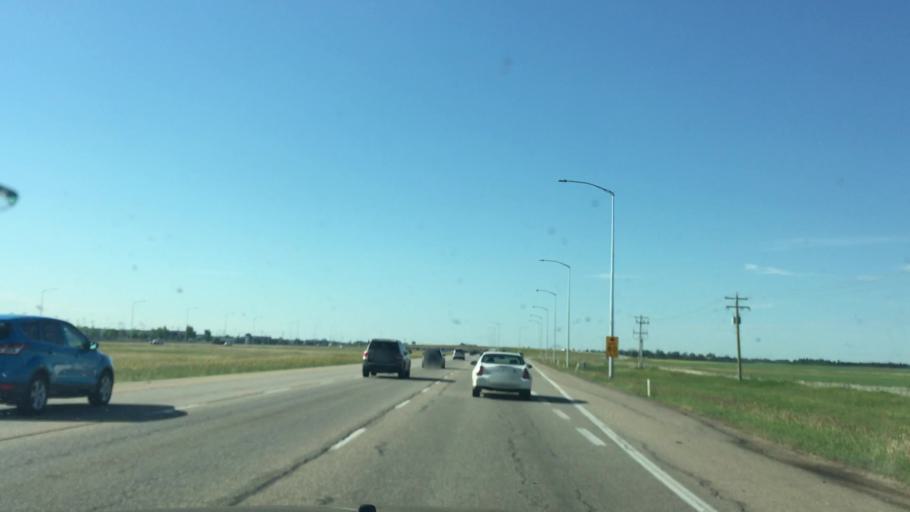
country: CA
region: Alberta
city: Leduc
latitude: 53.2938
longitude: -113.5499
